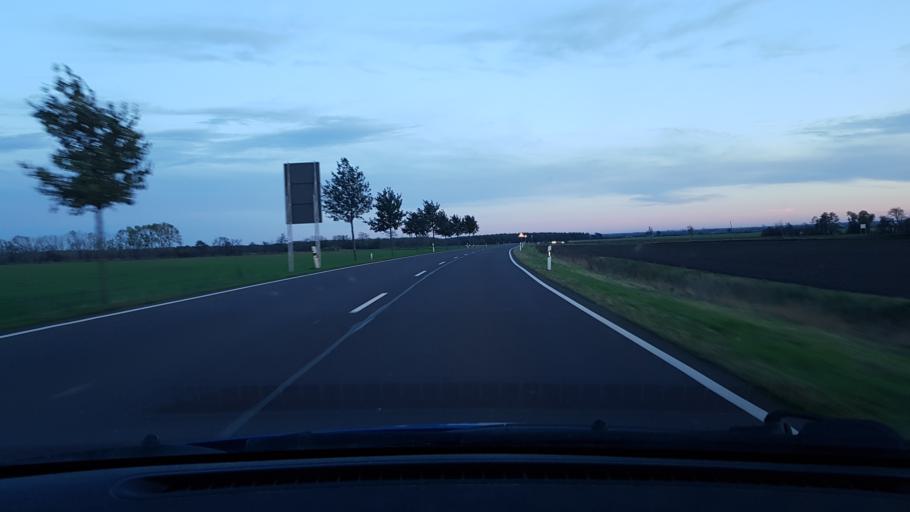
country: DE
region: Saxony-Anhalt
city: Leitzkau
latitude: 52.0466
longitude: 11.9698
